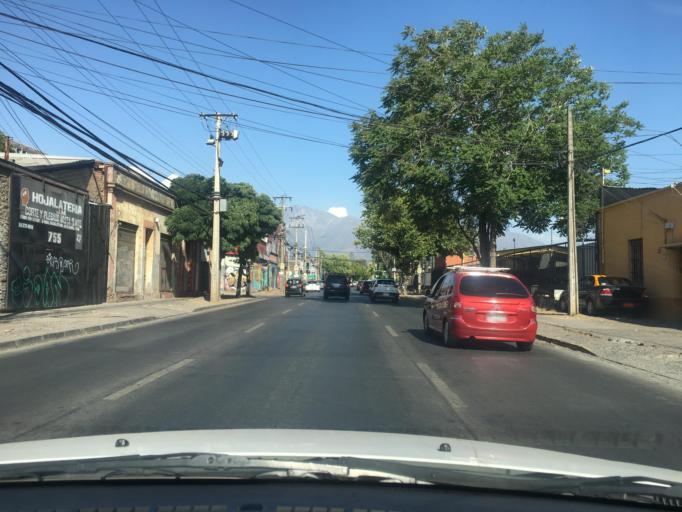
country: CL
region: Santiago Metropolitan
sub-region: Provincia de Santiago
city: Santiago
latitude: -33.4807
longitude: -70.6430
